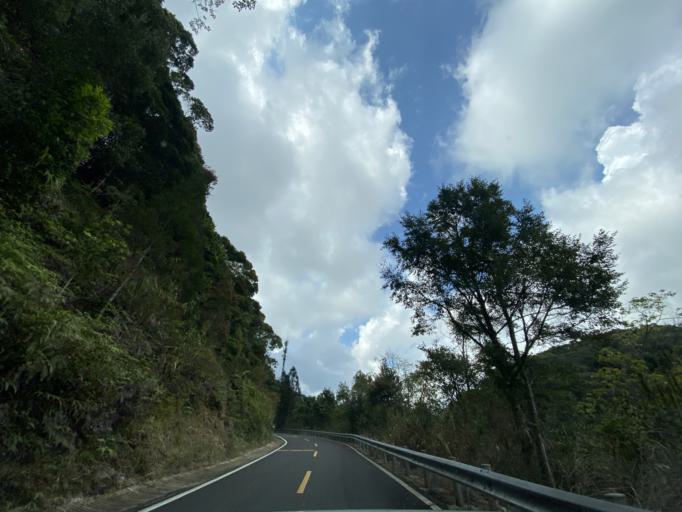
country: CN
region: Hainan
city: Diaoluoshan
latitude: 18.7190
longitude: 109.8777
